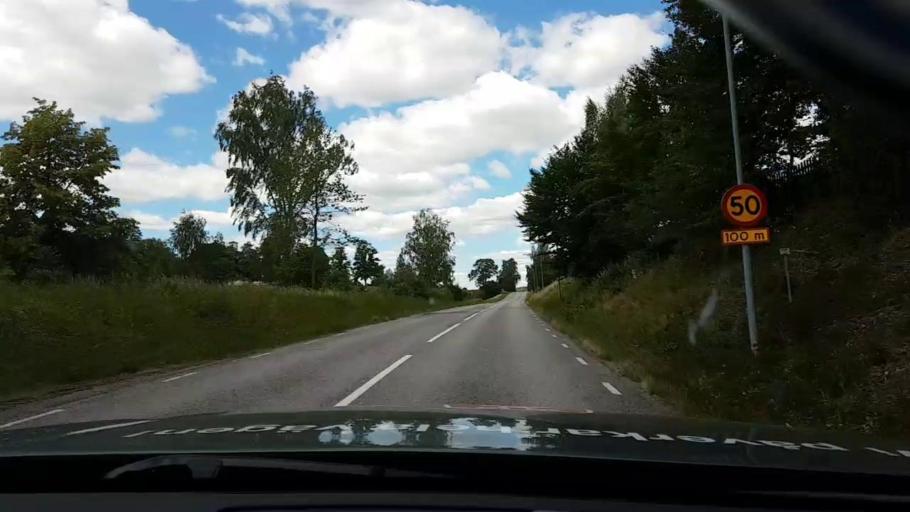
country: SE
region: Kalmar
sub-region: Vasterviks Kommun
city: Overum
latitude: 58.0779
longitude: 16.3573
